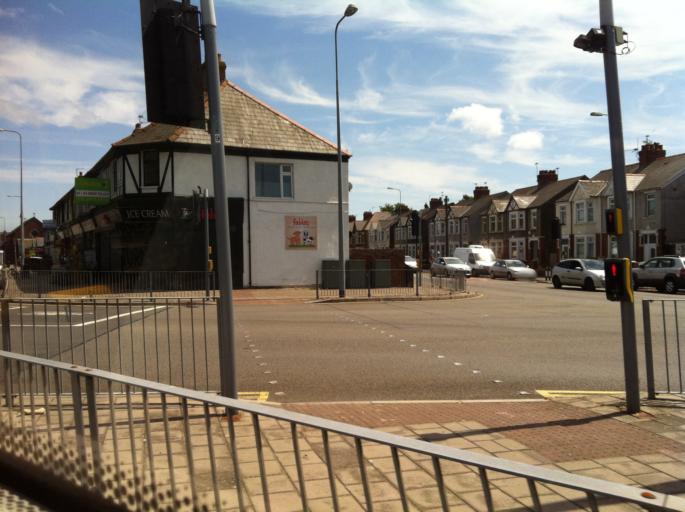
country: GB
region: Wales
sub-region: Cardiff
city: Cardiff
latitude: 51.4829
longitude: -3.2198
